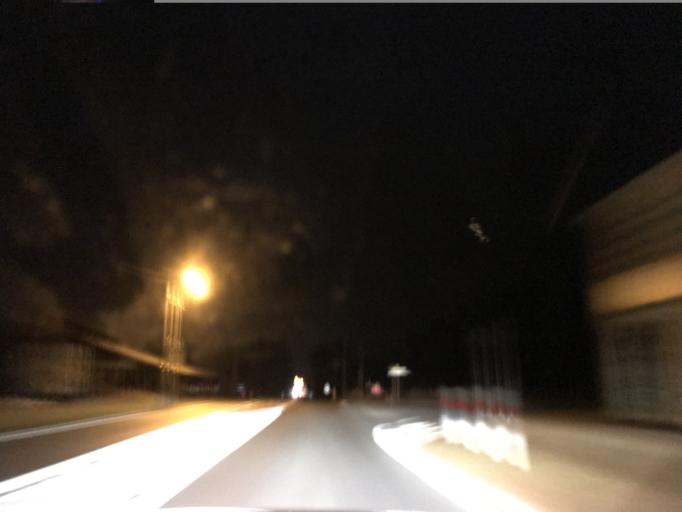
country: FR
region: Auvergne
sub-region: Departement du Puy-de-Dome
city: Puy-Guillaume
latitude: 45.9900
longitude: 3.4864
